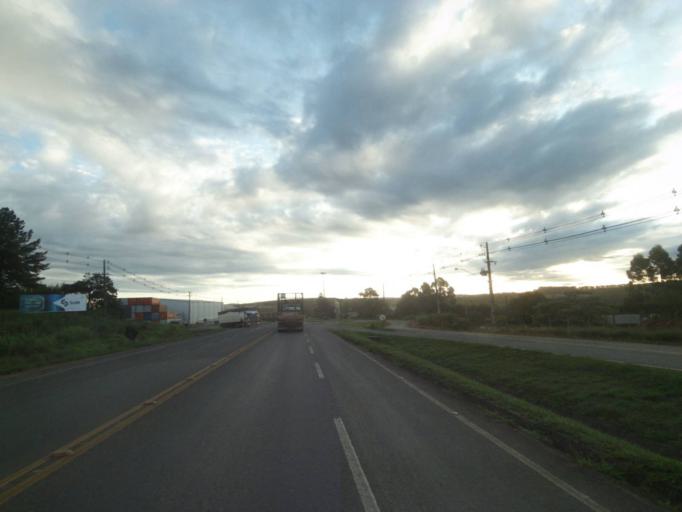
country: BR
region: Parana
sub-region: Telemaco Borba
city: Telemaco Borba
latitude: -24.3795
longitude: -50.6694
